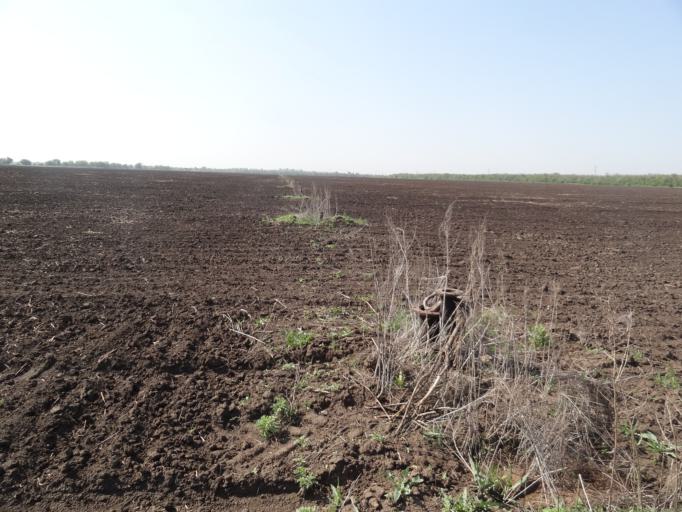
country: RU
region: Saratov
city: Engel's
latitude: 51.4226
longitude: 46.1140
